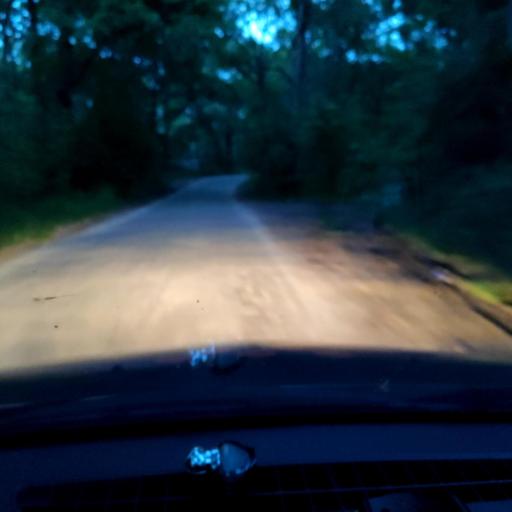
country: RU
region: Voronezj
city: Ramon'
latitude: 51.8307
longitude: 39.2720
